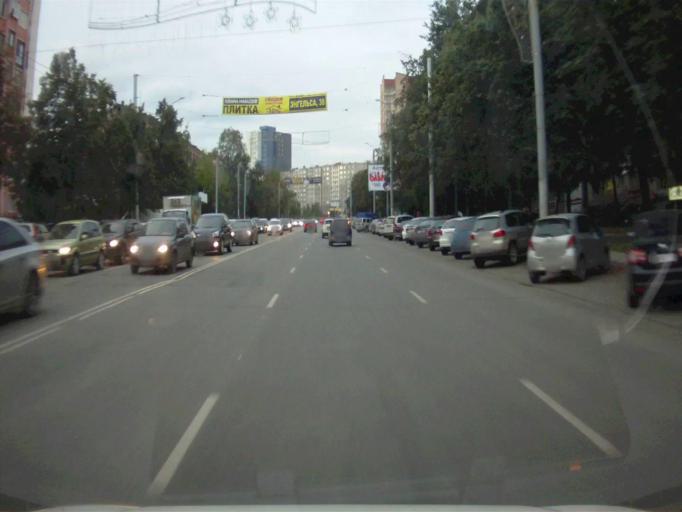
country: RU
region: Chelyabinsk
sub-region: Gorod Chelyabinsk
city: Chelyabinsk
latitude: 55.1566
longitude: 61.3814
